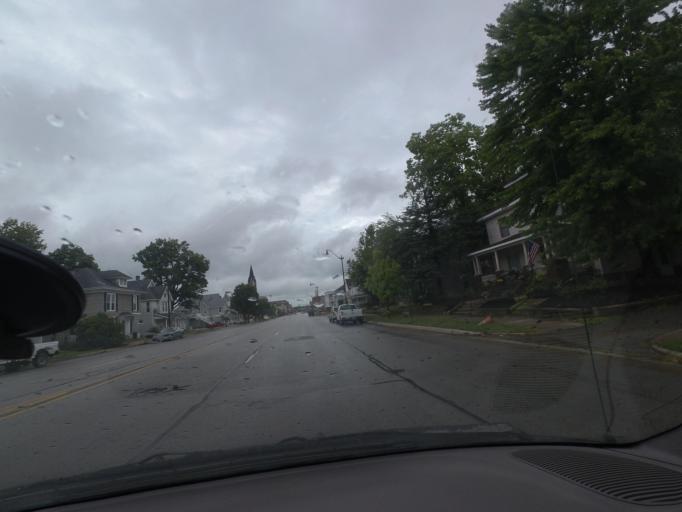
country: US
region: Indiana
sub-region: Montgomery County
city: Crawfordsville
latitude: 40.0376
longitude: -86.9013
